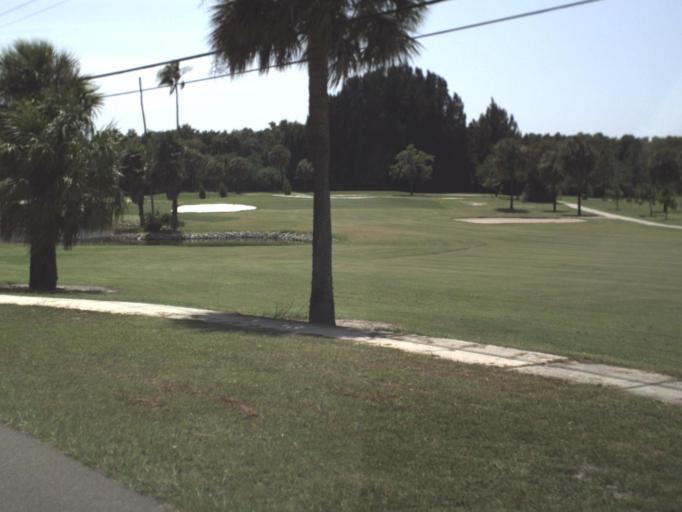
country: US
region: Florida
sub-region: Pinellas County
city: Tarpon Springs
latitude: 28.1317
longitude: -82.7588
